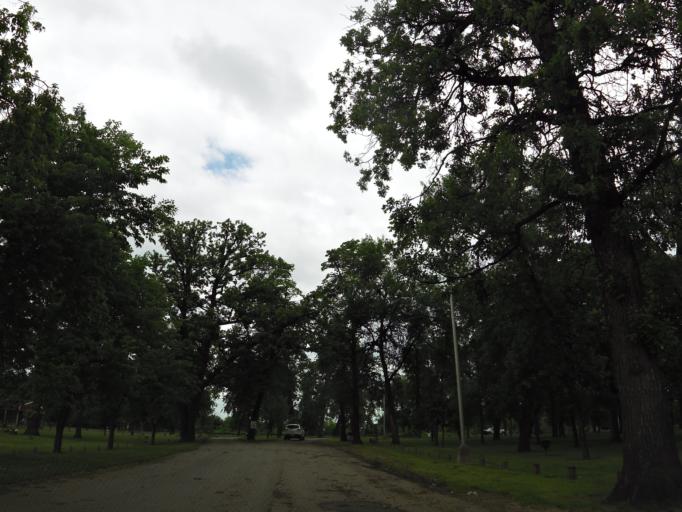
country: US
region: North Dakota
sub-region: Walsh County
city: Grafton
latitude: 48.4212
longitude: -97.4192
